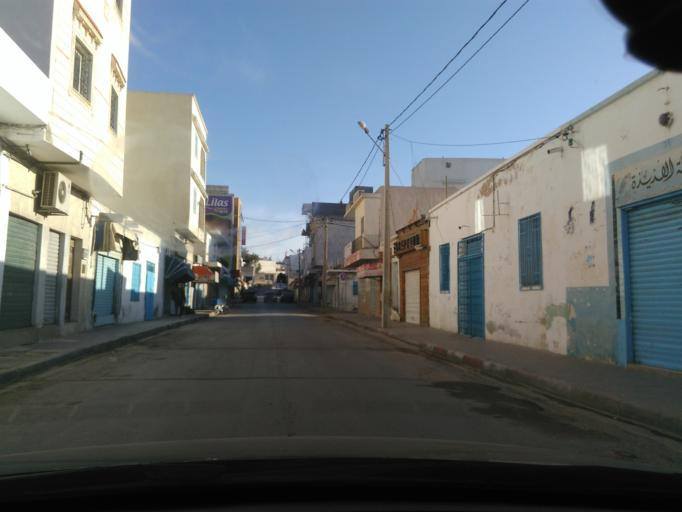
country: TN
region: Tataouine
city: Tataouine
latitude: 32.9287
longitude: 10.4484
